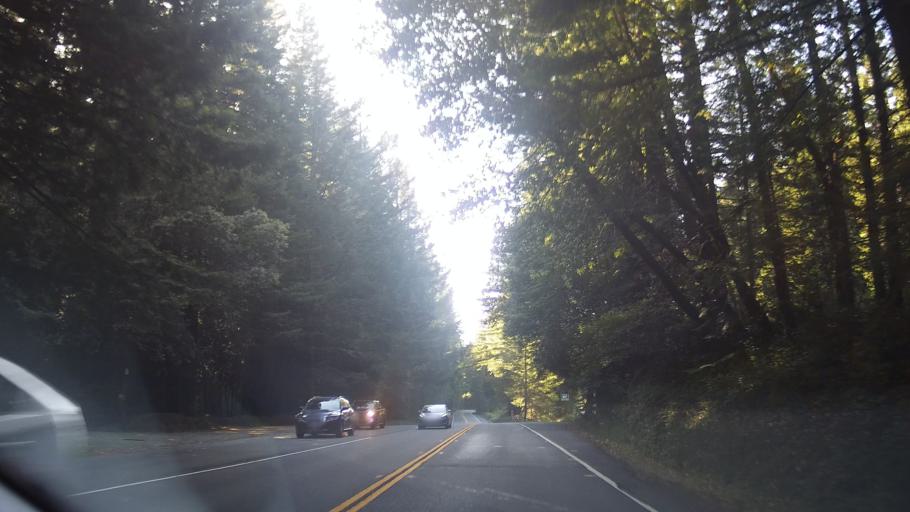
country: US
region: California
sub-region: Mendocino County
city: Fort Bragg
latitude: 39.3487
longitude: -123.6021
